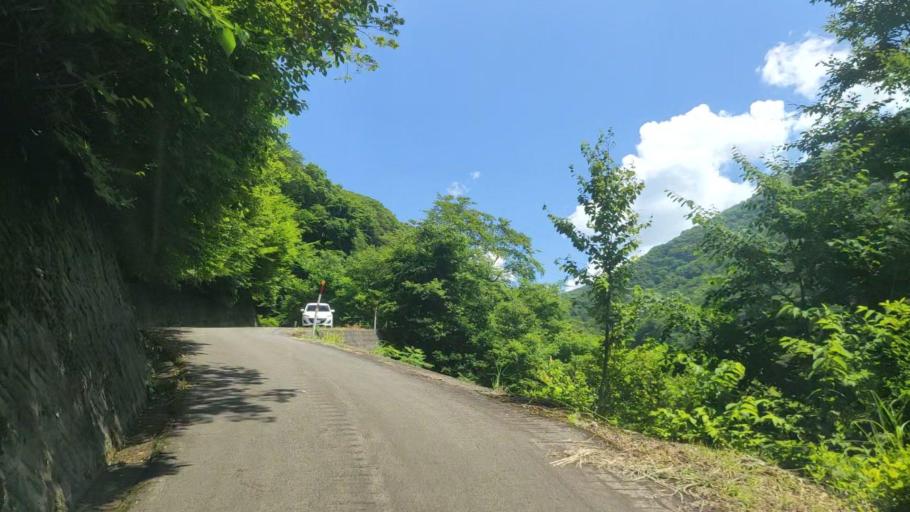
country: JP
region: Fukui
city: Ono
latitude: 35.7908
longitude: 136.5029
